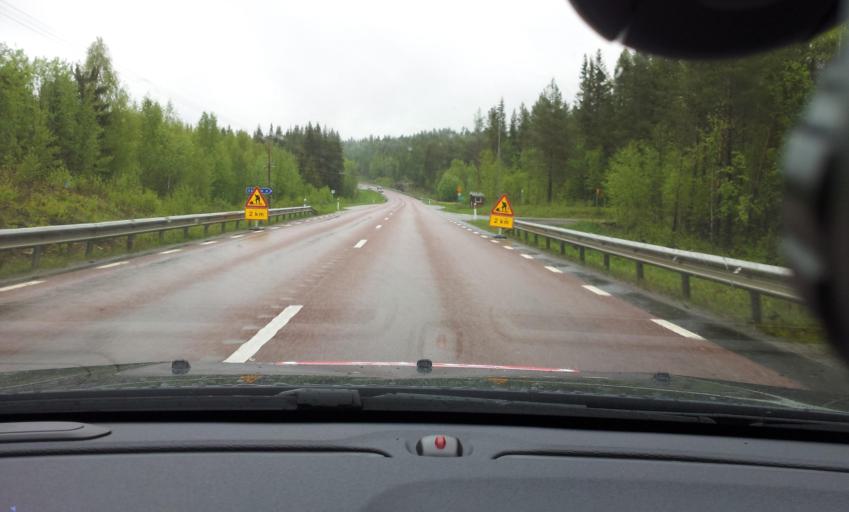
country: SE
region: Jaemtland
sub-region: Bergs Kommun
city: Hoverberg
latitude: 62.8691
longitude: 14.5212
